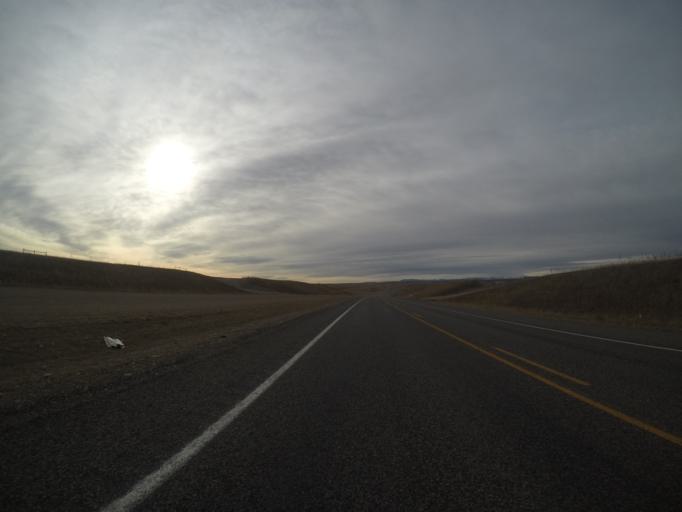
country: US
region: Montana
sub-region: Yellowstone County
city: Laurel
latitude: 45.5747
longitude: -108.8458
